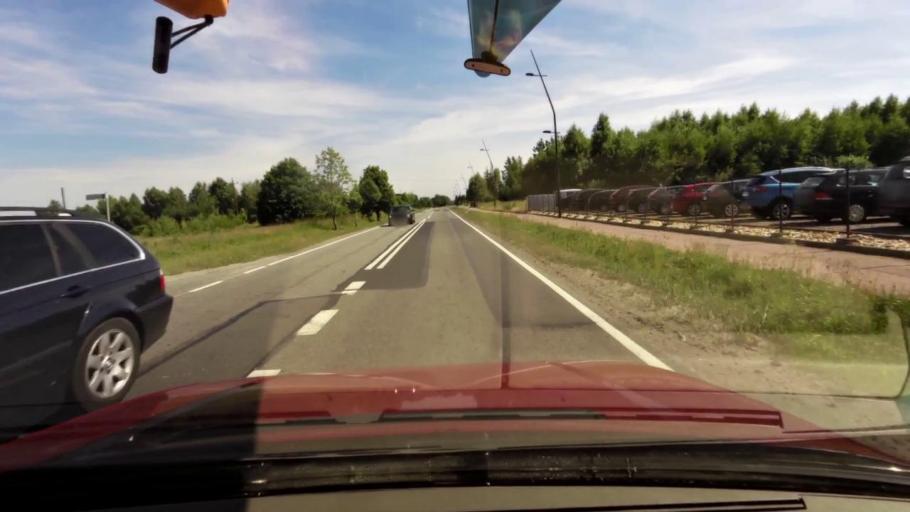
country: PL
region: Pomeranian Voivodeship
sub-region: Powiat slupski
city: Kobylnica
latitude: 54.4327
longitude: 17.0019
